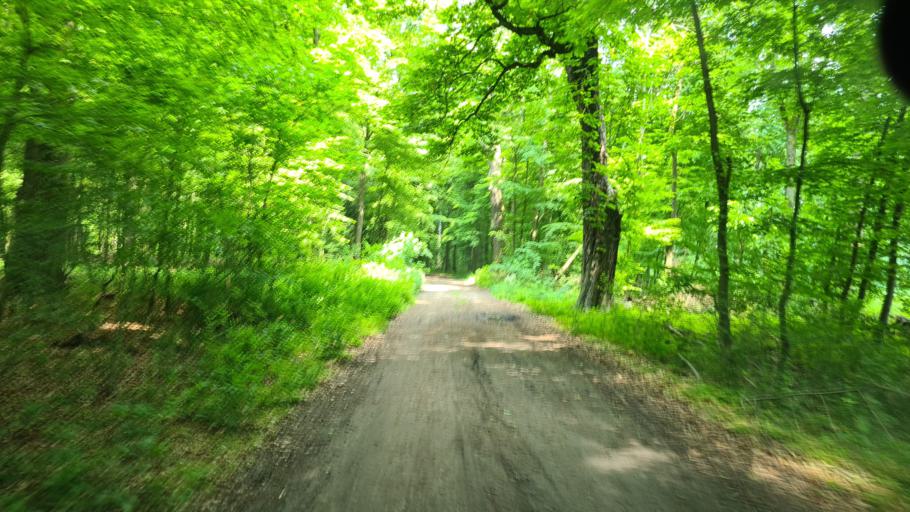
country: DE
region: Brandenburg
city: Sonnewalde
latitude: 51.7013
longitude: 13.6382
